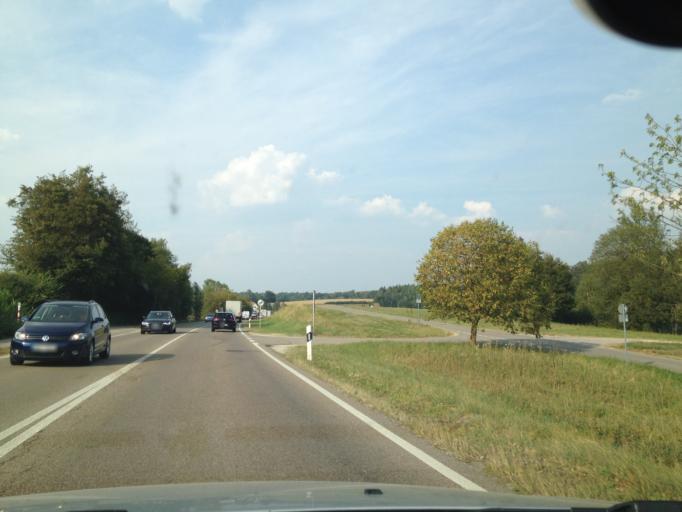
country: DE
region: Bavaria
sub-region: Swabia
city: Buchdorf
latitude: 48.8098
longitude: 10.8248
